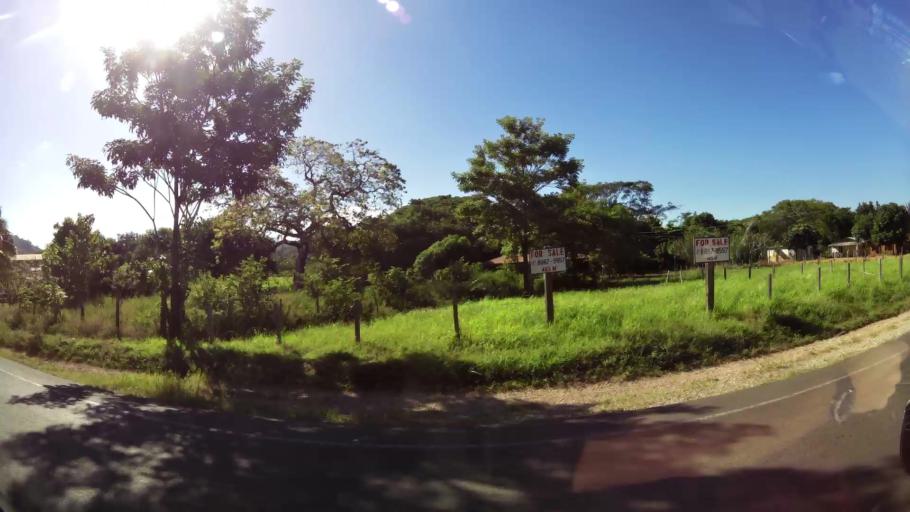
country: CR
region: Guanacaste
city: Belen
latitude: 10.3704
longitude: -85.7799
